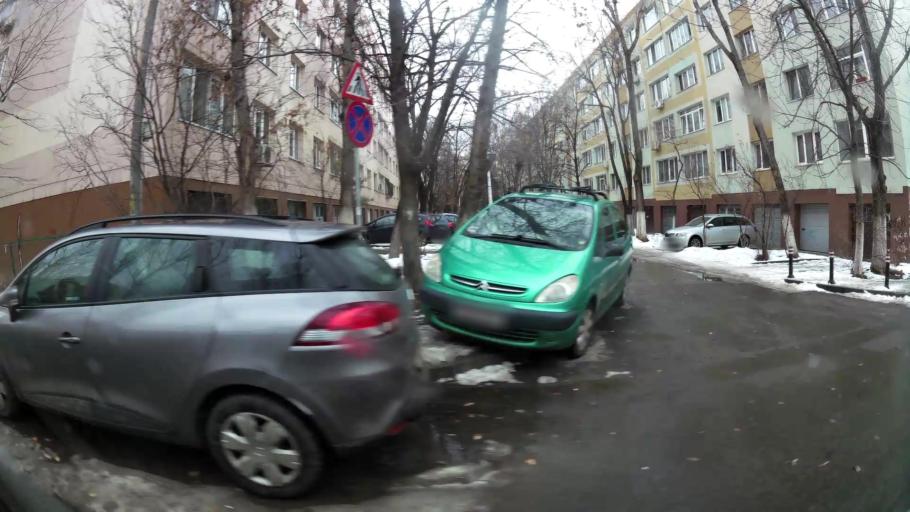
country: RO
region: Ilfov
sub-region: Comuna Chiajna
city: Rosu
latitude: 44.4213
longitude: 26.0256
